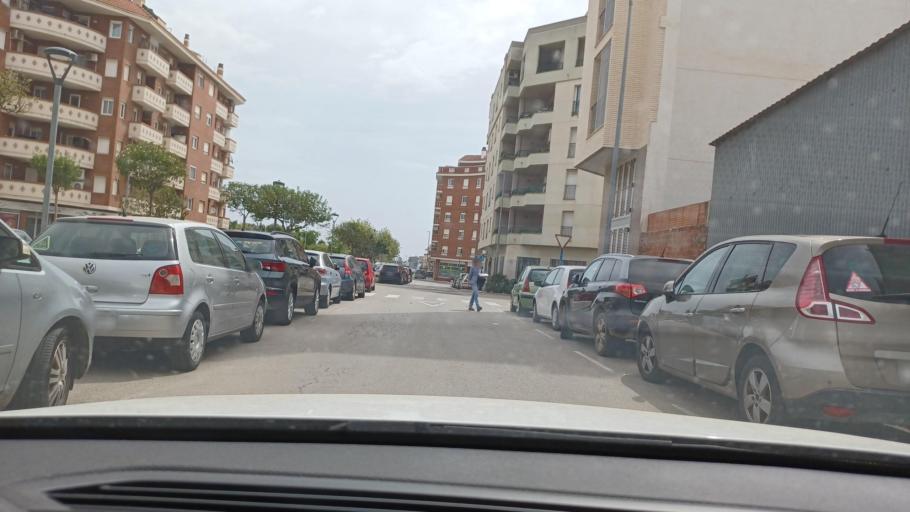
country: ES
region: Catalonia
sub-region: Provincia de Tarragona
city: Amposta
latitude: 40.7037
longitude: 0.5807
